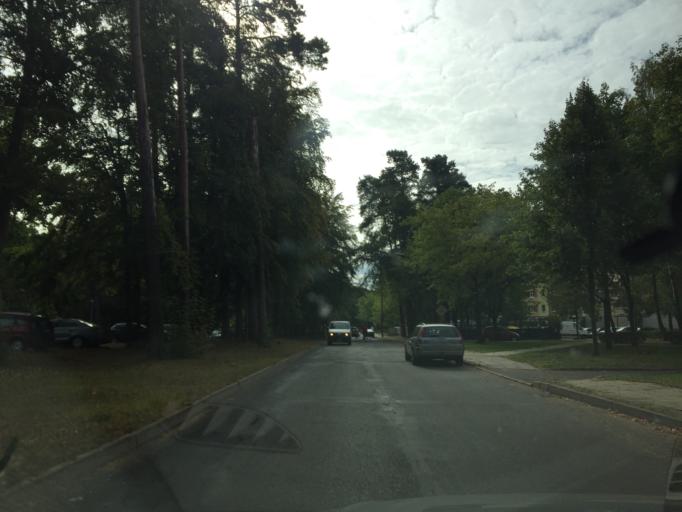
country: DE
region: Brandenburg
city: Erkner
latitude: 52.4151
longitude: 13.7618
